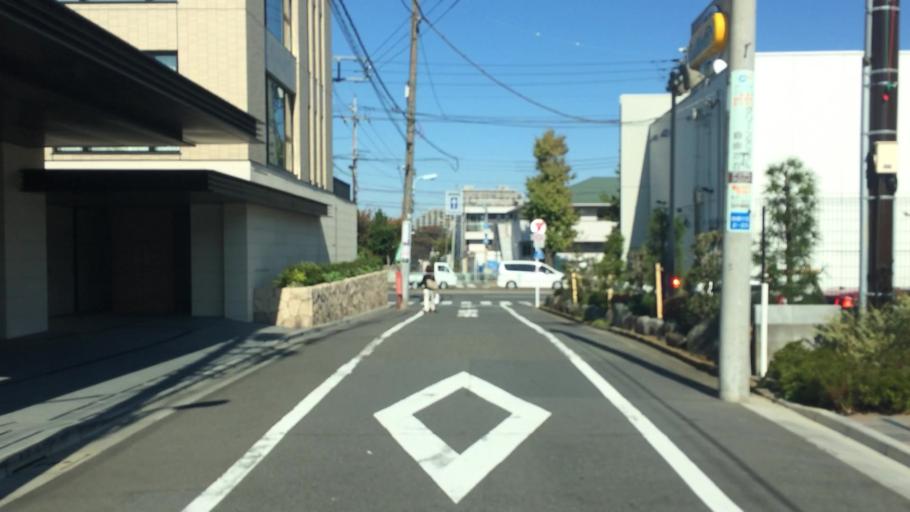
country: JP
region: Tokyo
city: Tokyo
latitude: 35.6134
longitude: 139.6655
